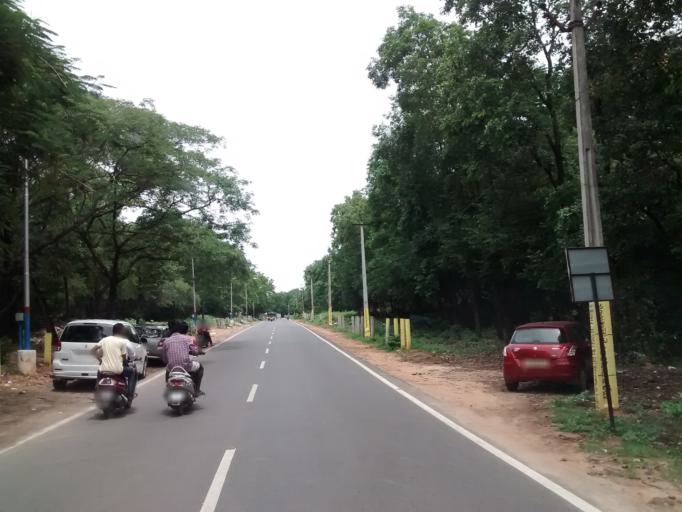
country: IN
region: Andhra Pradesh
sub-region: Chittoor
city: Akkarampalle
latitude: 13.6463
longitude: 79.4051
